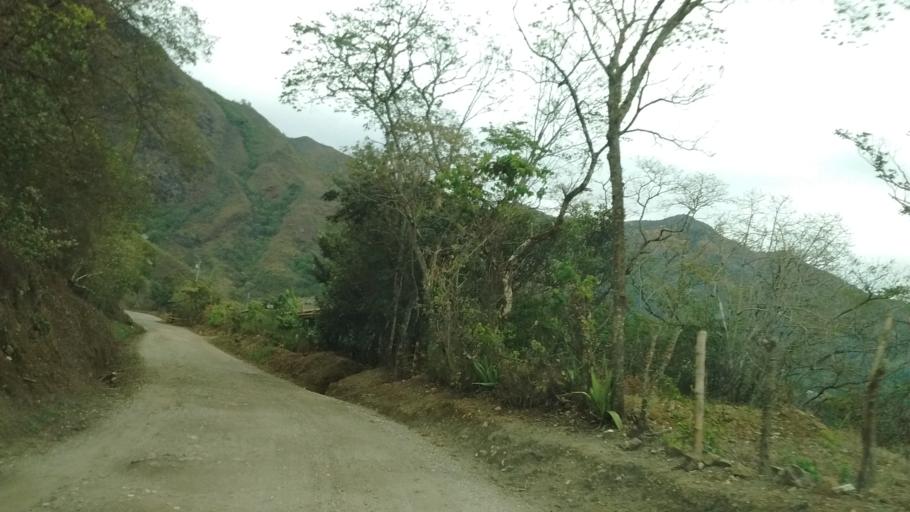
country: CO
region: Cauca
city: Almaguer
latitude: 1.8451
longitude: -76.9057
